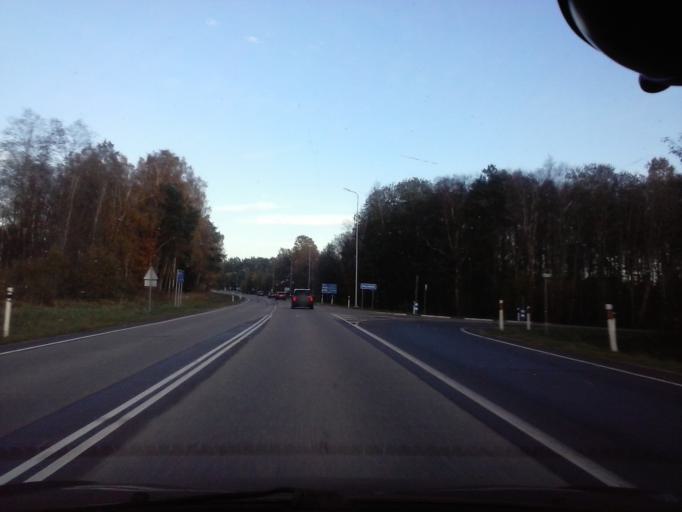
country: EE
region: Laeaene
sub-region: Ridala Parish
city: Uuemoisa
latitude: 58.9709
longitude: 23.8786
